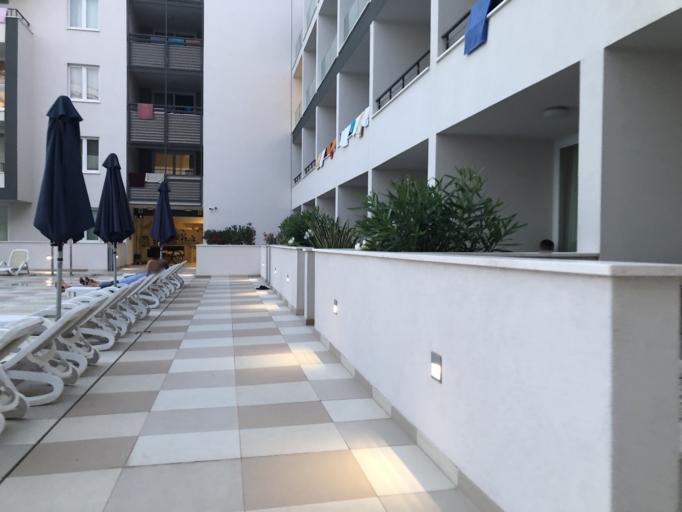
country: HR
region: Splitsko-Dalmatinska
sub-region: Grad Makarska
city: Makarska
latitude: 43.3072
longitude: 17.0025
